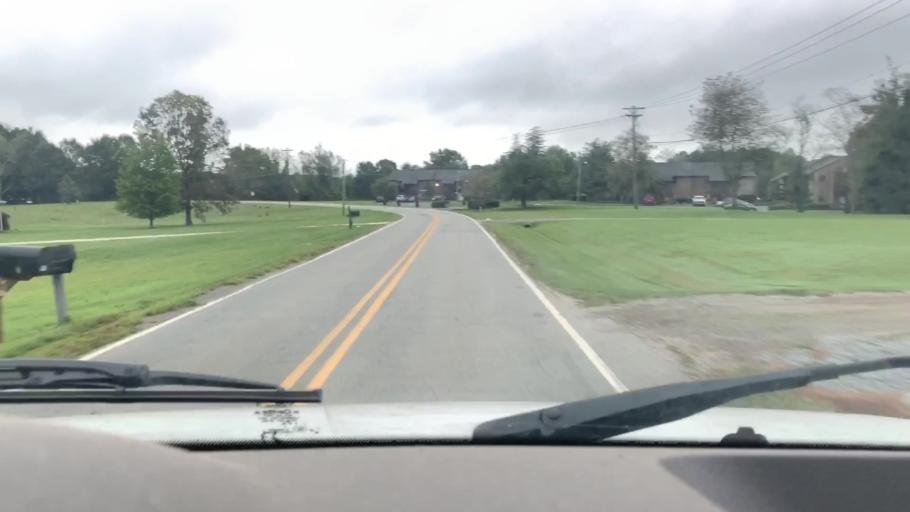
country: US
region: North Carolina
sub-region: Catawba County
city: Lake Norman of Catawba
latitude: 35.5642
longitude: -80.9025
